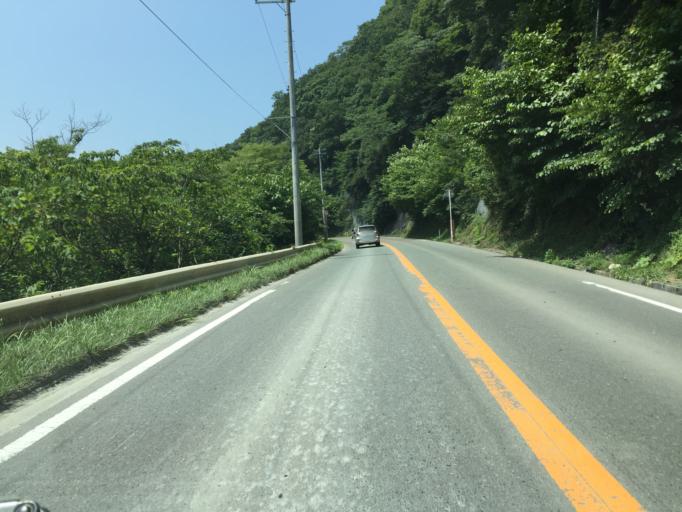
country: JP
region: Miyagi
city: Marumori
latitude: 37.8495
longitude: 140.8593
